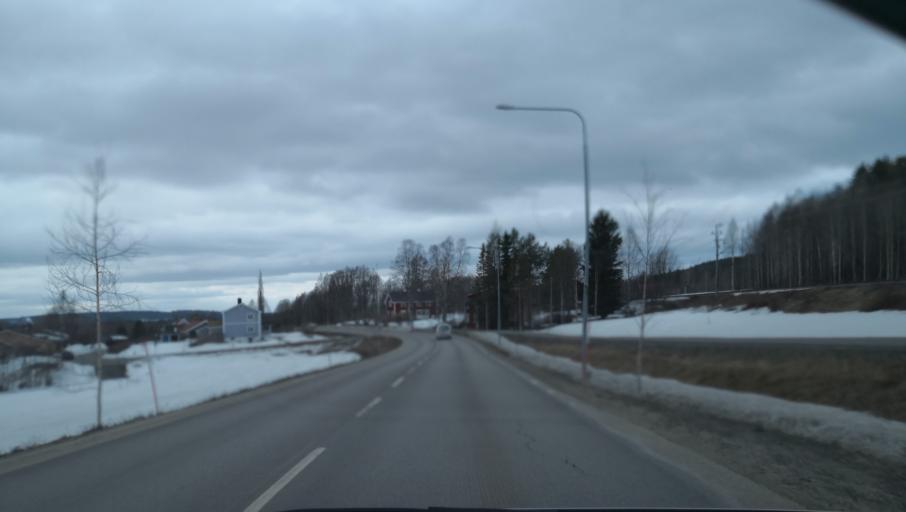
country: SE
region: Vaesterbotten
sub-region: Vannas Kommun
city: Vannasby
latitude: 63.9165
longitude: 19.8013
